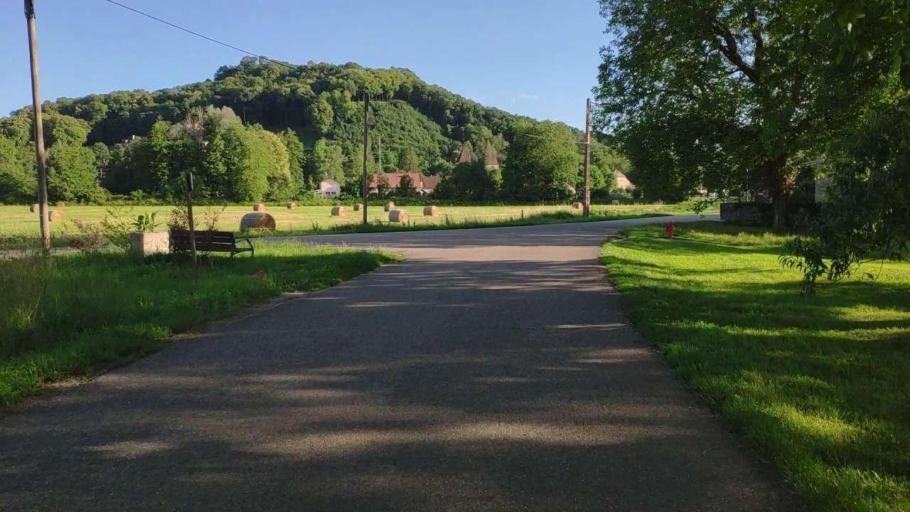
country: FR
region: Franche-Comte
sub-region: Departement du Jura
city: Bletterans
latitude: 46.7635
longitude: 5.5375
